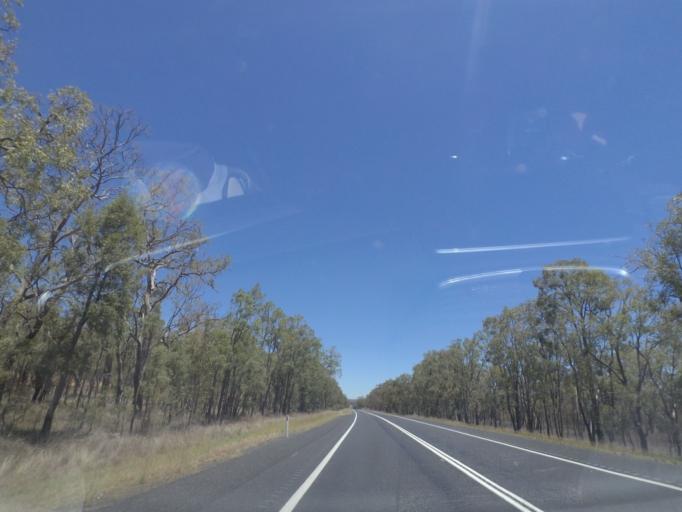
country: AU
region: New South Wales
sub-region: Warrumbungle Shire
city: Coonabarabran
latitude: -31.2099
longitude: 149.3308
